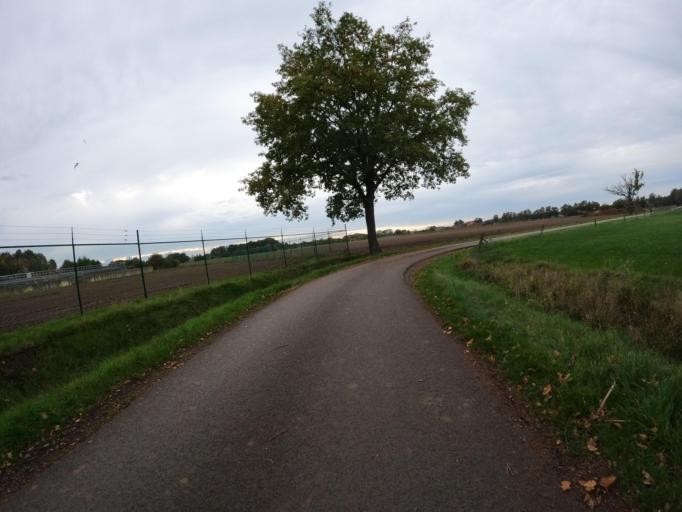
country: BE
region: Flanders
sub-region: Provincie Antwerpen
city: Hulshout
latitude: 51.1138
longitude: 4.8066
